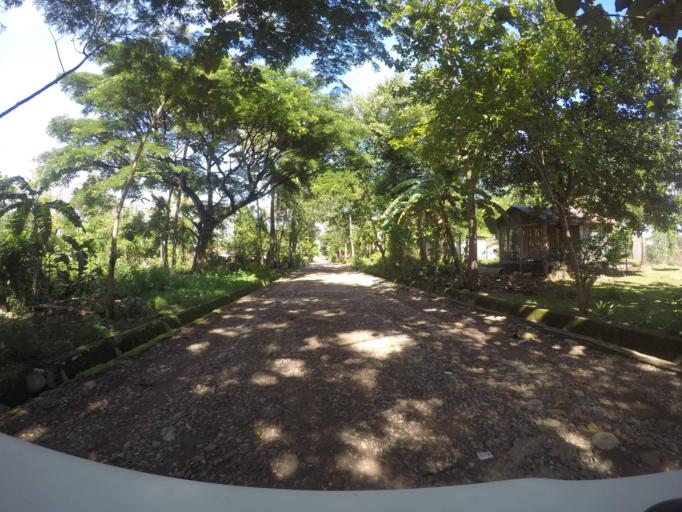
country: TL
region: Bobonaro
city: Maliana
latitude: -8.9880
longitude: 125.2051
